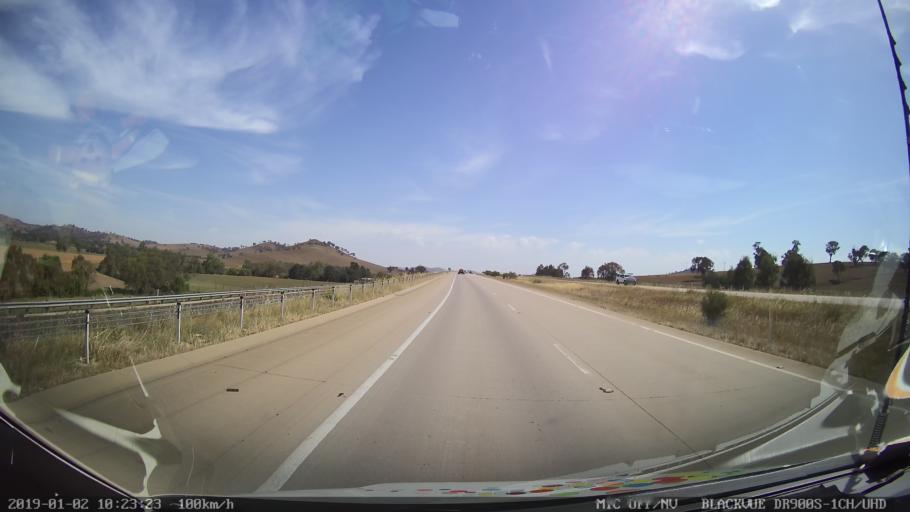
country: AU
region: New South Wales
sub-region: Gundagai
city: Gundagai
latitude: -34.9597
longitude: 148.1564
